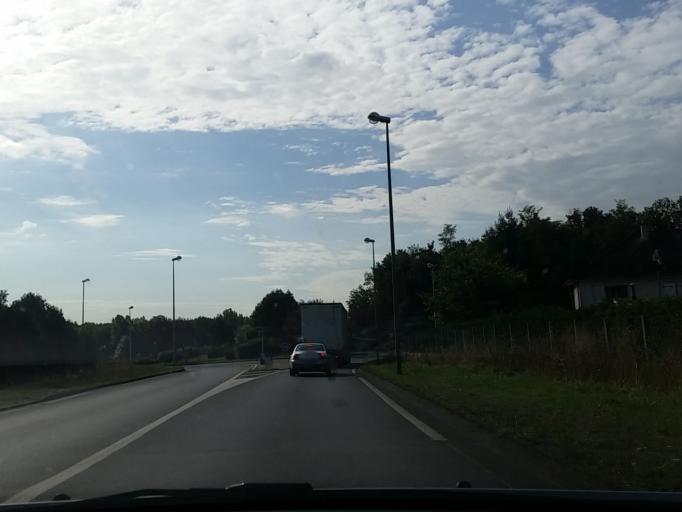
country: FR
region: Centre
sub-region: Departement du Loir-et-Cher
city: Romorantin-Lanthenay
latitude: 47.3508
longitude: 1.7229
